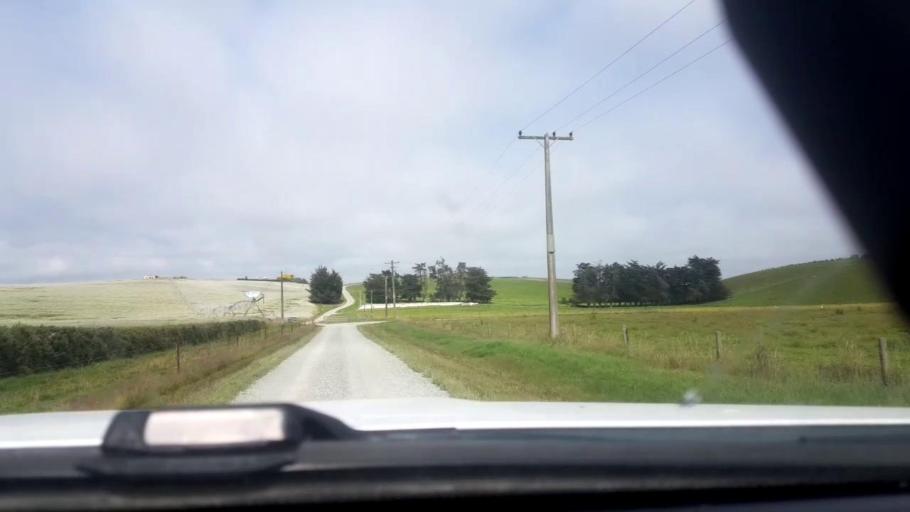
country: NZ
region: Canterbury
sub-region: Timaru District
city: Timaru
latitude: -44.3306
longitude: 171.2008
